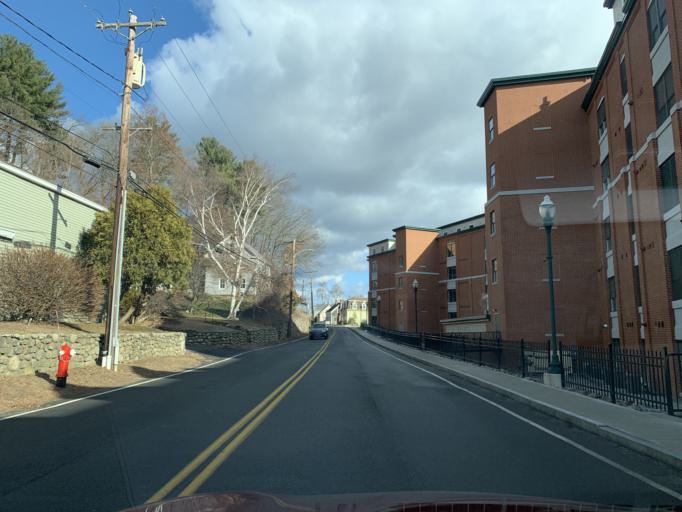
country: US
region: Massachusetts
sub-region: Essex County
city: Amesbury
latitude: 42.8368
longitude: -70.9296
